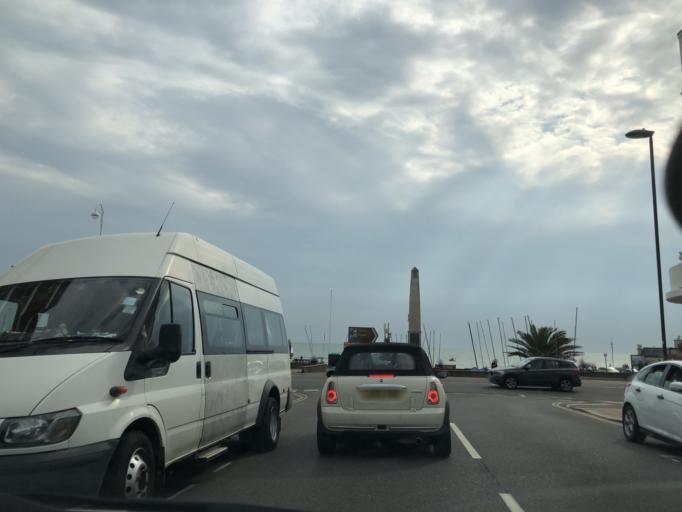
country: GB
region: England
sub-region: East Sussex
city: Bexhill-on-Sea
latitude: 50.8384
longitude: 0.4768
